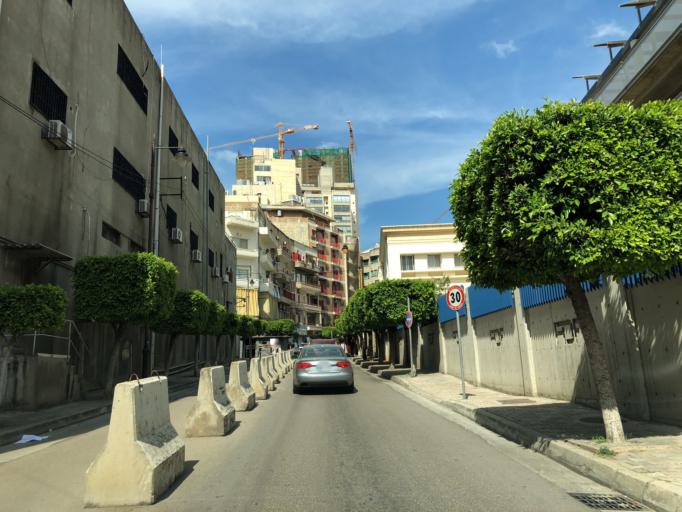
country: LB
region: Beyrouth
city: Beirut
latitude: 33.8810
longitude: 35.5175
